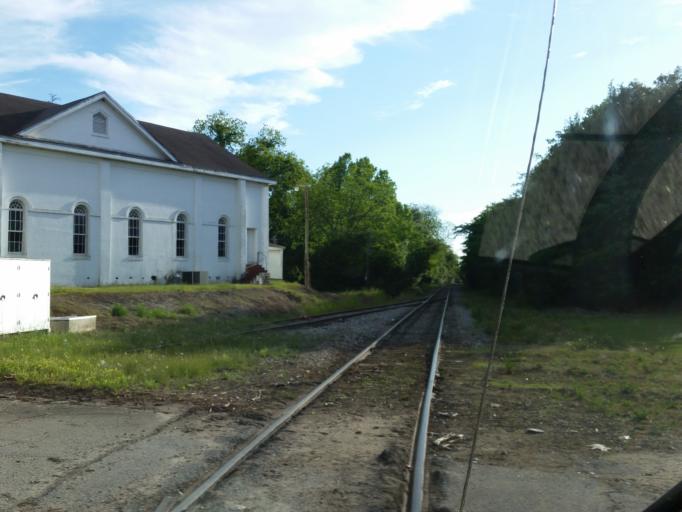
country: US
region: Georgia
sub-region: Crisp County
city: Cordele
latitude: 31.9685
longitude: -83.7881
